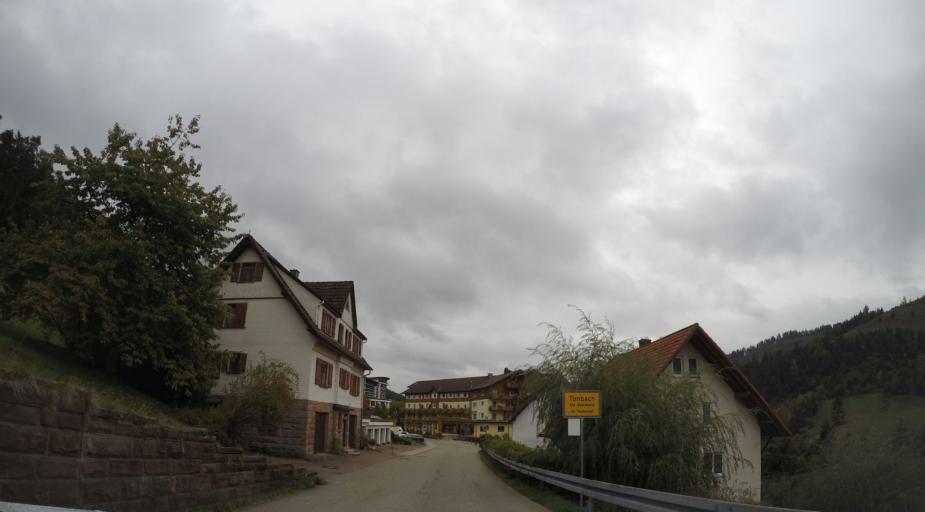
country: DE
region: Baden-Wuerttemberg
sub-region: Karlsruhe Region
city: Baiersbronn
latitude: 48.5392
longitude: 8.3560
